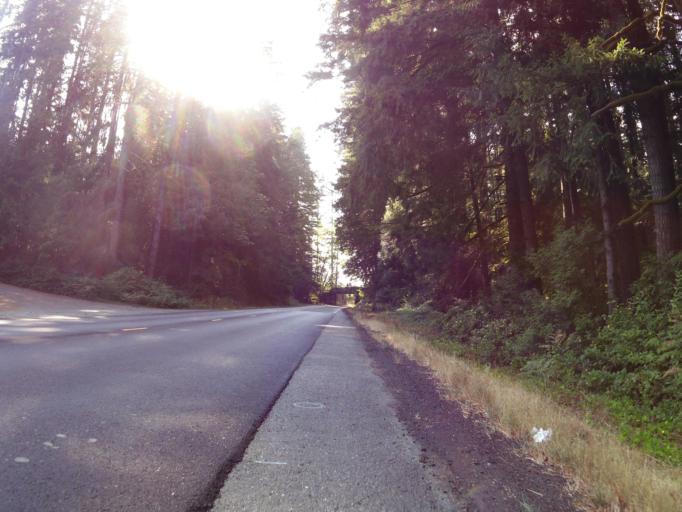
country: US
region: Washington
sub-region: Kitsap County
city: Erlands Point-Kitsap Lake
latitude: 47.5250
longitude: -122.7538
